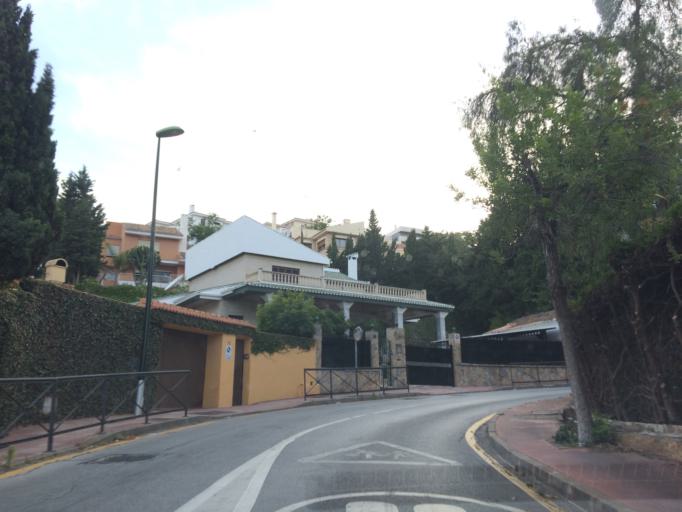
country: ES
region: Andalusia
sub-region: Provincia de Malaga
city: Malaga
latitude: 36.7265
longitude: -4.3840
